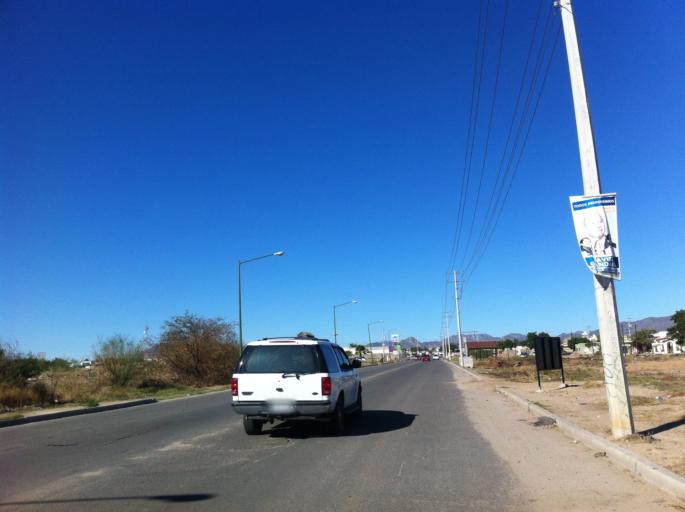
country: MX
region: Sonora
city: Hermosillo
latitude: 29.1123
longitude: -111.0056
